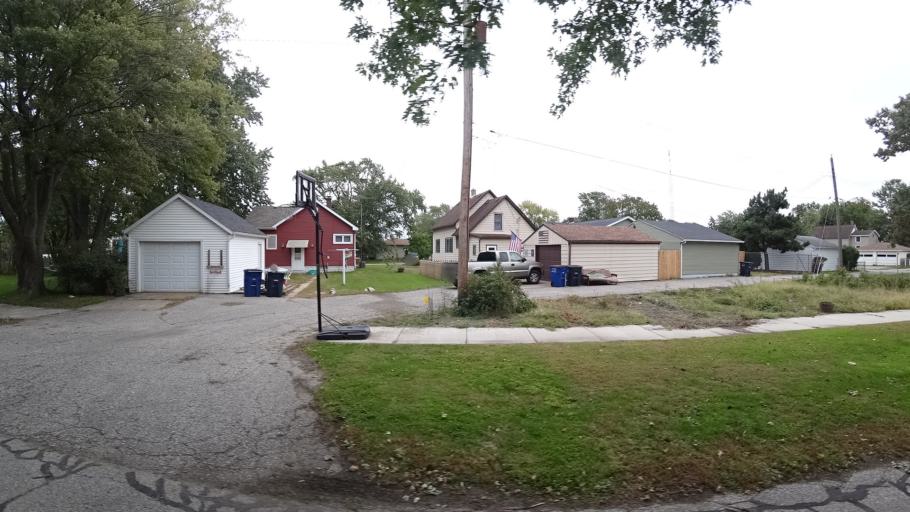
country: US
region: Indiana
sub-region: LaPorte County
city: Michigan City
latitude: 41.7000
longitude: -86.8984
